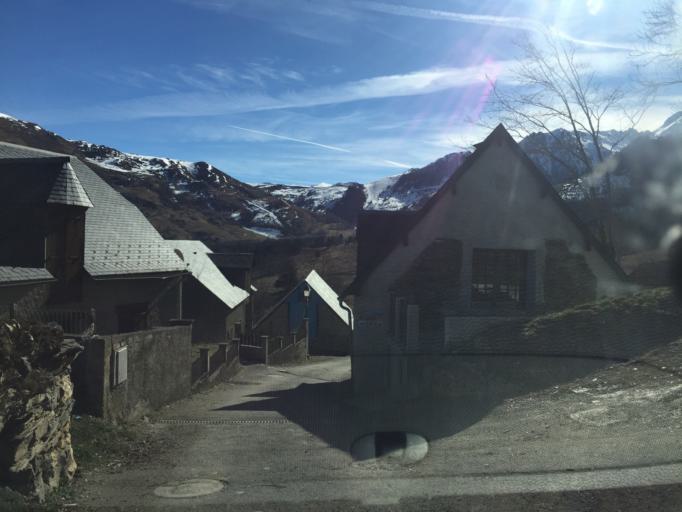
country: FR
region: Midi-Pyrenees
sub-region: Departement des Hautes-Pyrenees
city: Saint-Lary-Soulan
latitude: 42.8072
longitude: 0.3390
